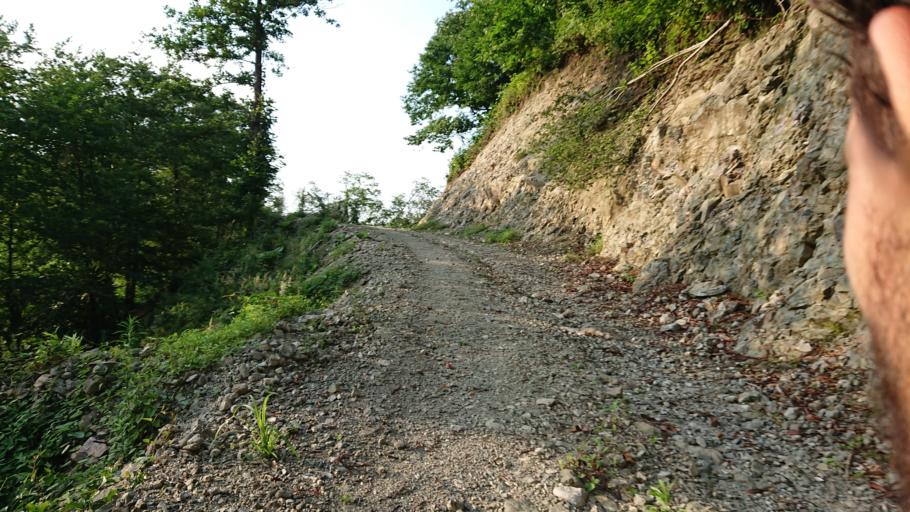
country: TR
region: Rize
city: Rize
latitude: 40.9898
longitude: 40.5051
